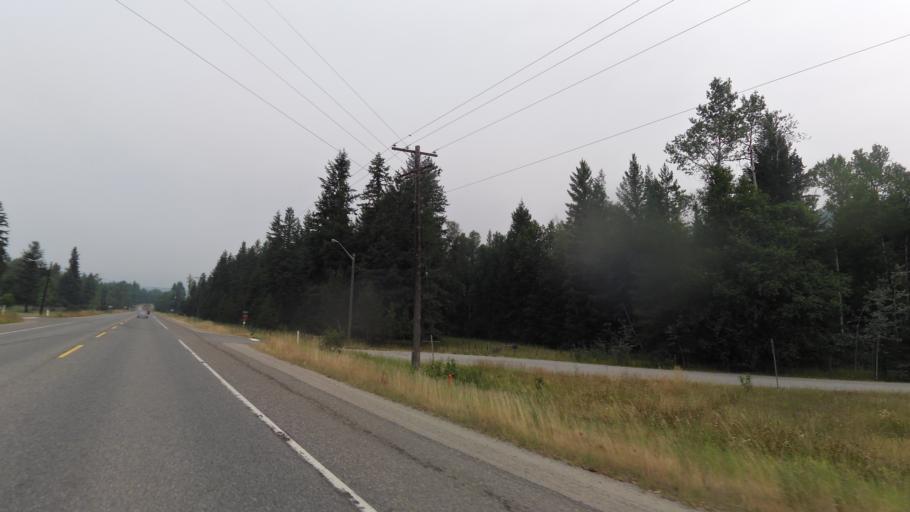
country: CA
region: British Columbia
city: Chase
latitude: 51.6365
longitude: -119.9704
